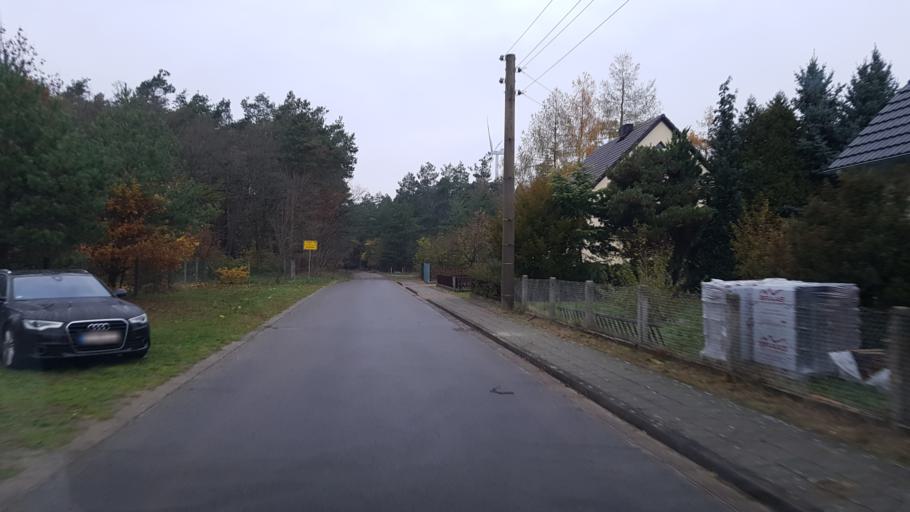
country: DE
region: Brandenburg
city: Schilda
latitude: 51.6483
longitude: 13.3866
